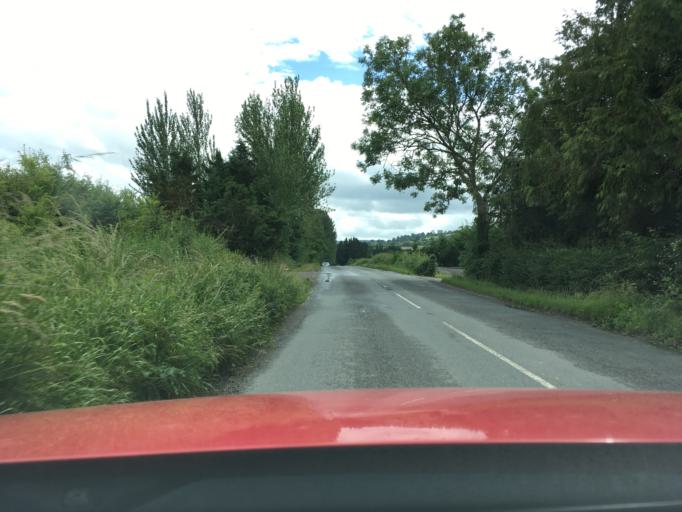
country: GB
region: England
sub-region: Gloucestershire
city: Winchcombe
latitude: 51.9844
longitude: -1.9730
